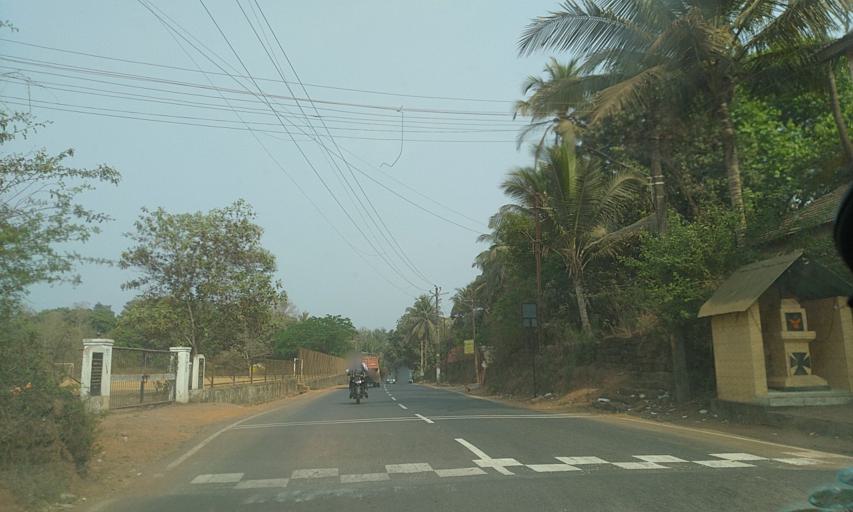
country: IN
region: Goa
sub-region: South Goa
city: Davorlim
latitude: 15.2607
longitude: 74.0457
